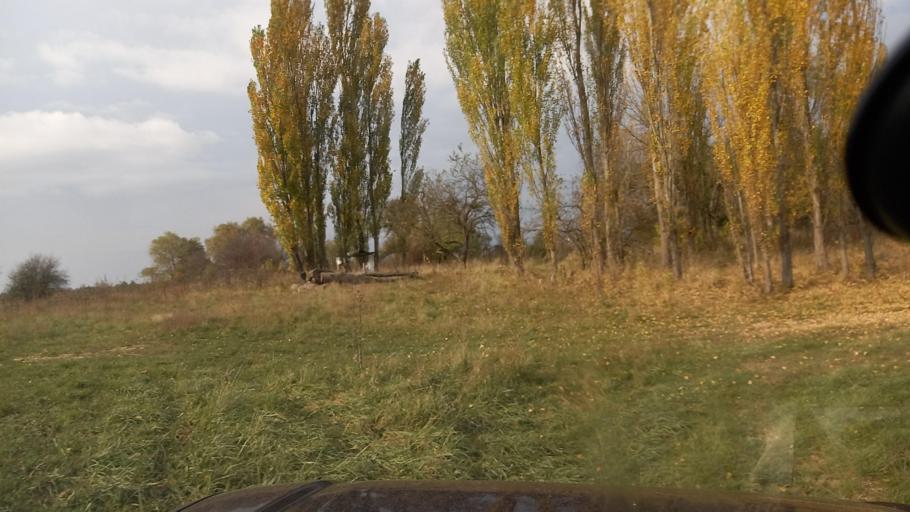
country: RU
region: Krasnodarskiy
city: Gubskaya
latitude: 44.3078
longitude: 40.5487
